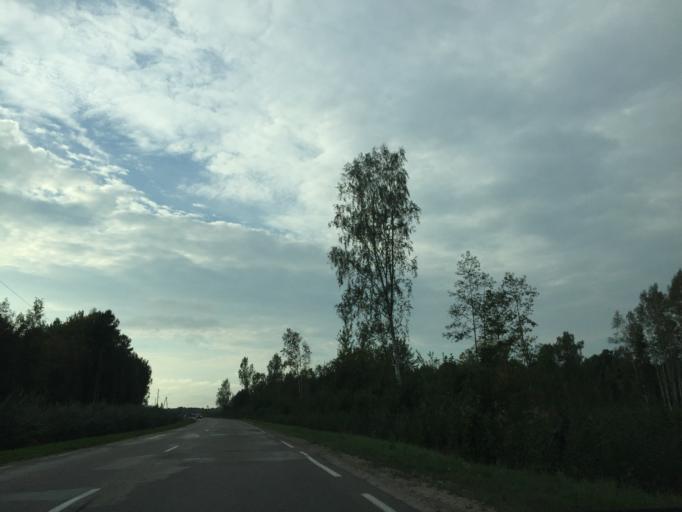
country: LV
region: Ikskile
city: Ikskile
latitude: 56.8151
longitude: 24.4728
